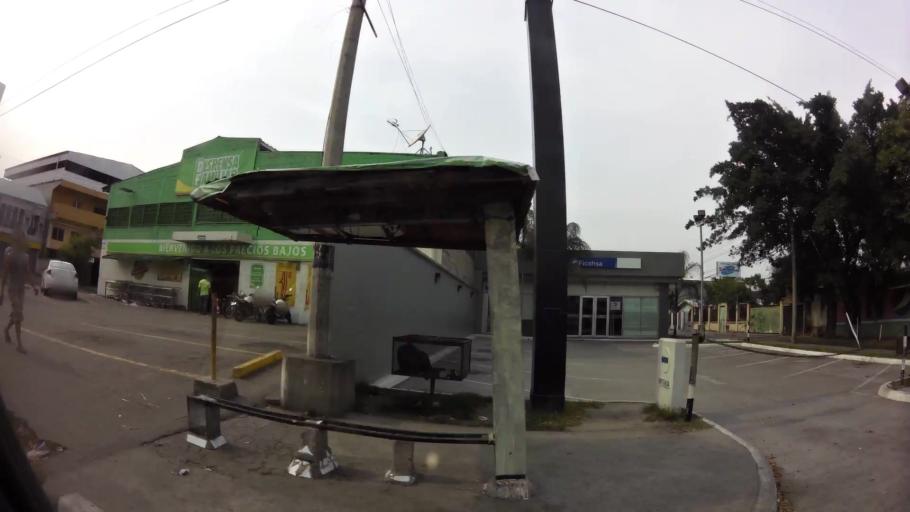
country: HN
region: Cortes
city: San Pedro Sula
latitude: 15.4993
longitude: -88.0156
